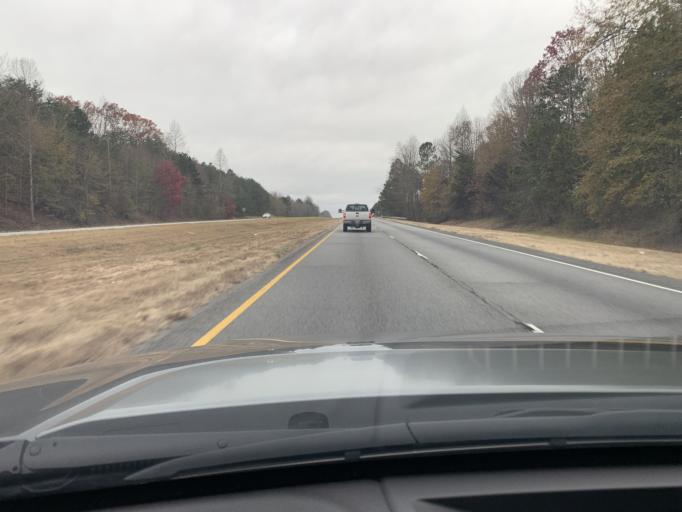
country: US
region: Georgia
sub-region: Hall County
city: Lula
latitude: 34.4125
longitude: -83.6631
